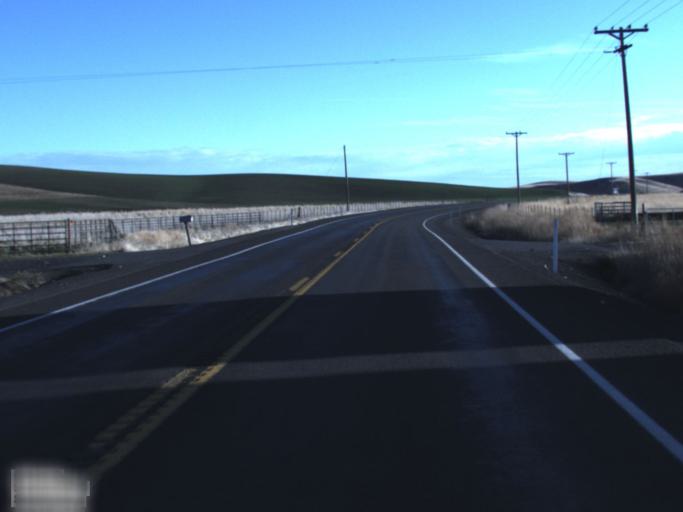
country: US
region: Washington
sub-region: Garfield County
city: Pomeroy
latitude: 46.7919
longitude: -117.6858
